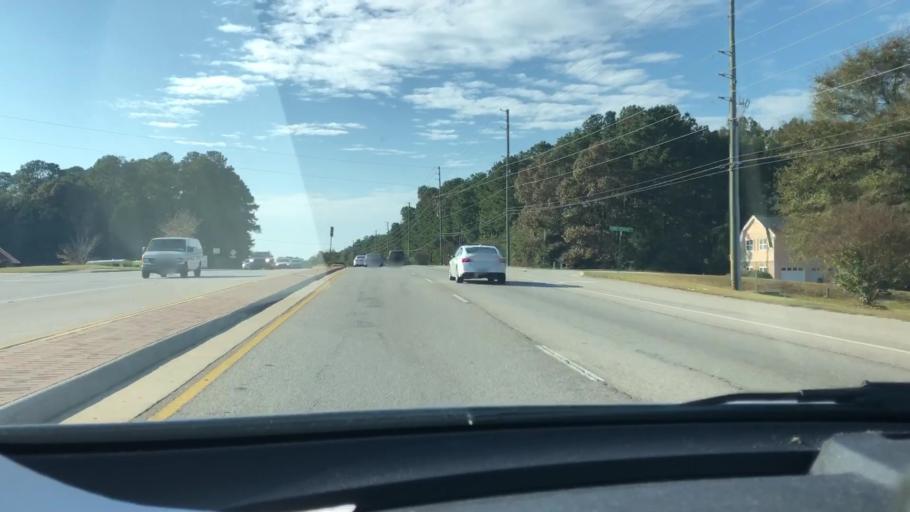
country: US
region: Georgia
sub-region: Henry County
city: McDonough
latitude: 33.4587
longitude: -84.1781
